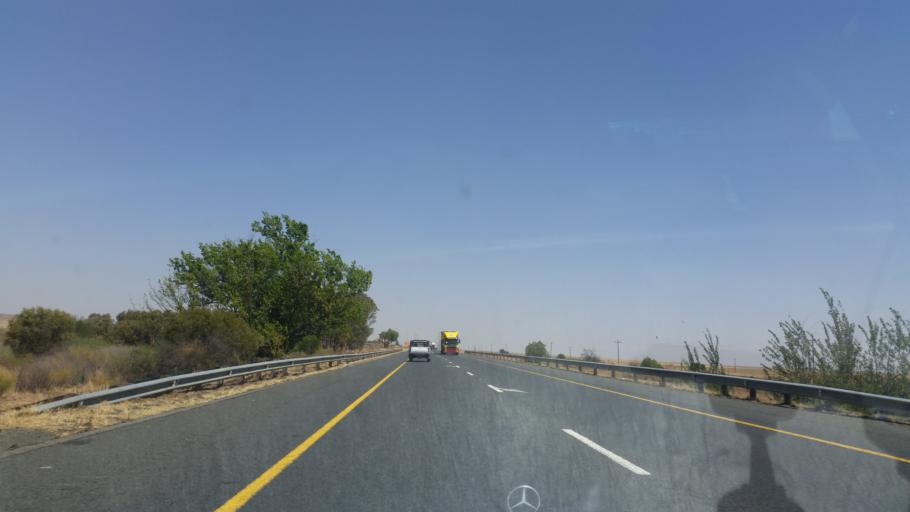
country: ZA
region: Orange Free State
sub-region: Lejweleputswa District Municipality
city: Brandfort
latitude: -28.7916
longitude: 26.6999
